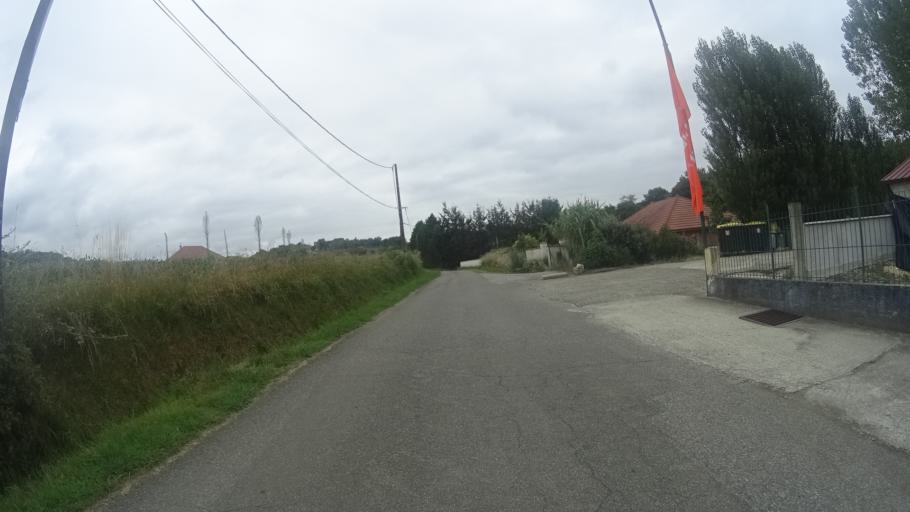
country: FR
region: Aquitaine
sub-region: Departement des Pyrenees-Atlantiques
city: Mont
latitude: 43.4869
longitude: -0.6961
